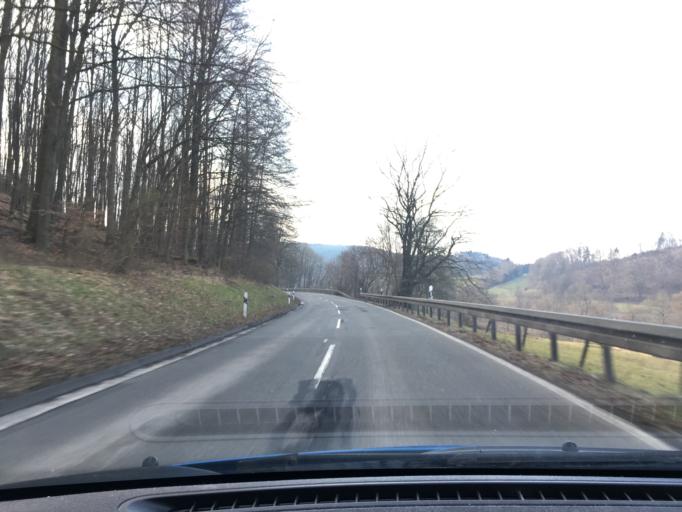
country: DE
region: Lower Saxony
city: Bodenfelde
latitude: 51.6258
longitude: 9.5953
